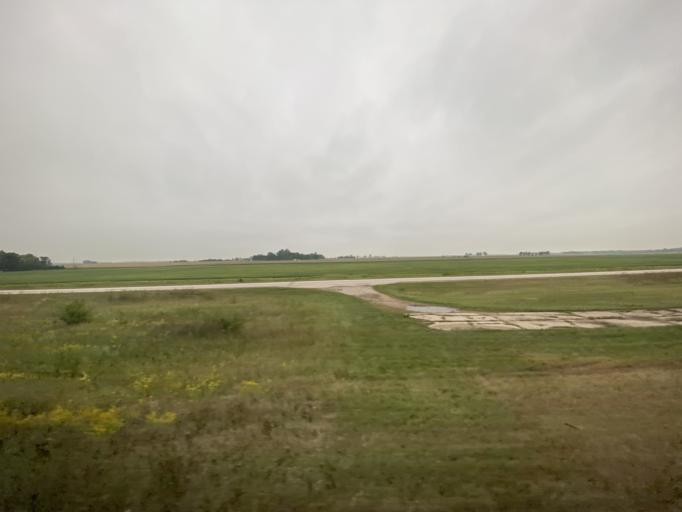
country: US
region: Illinois
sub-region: DeKalb County
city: Somonauk
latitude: 41.6250
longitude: -88.7347
